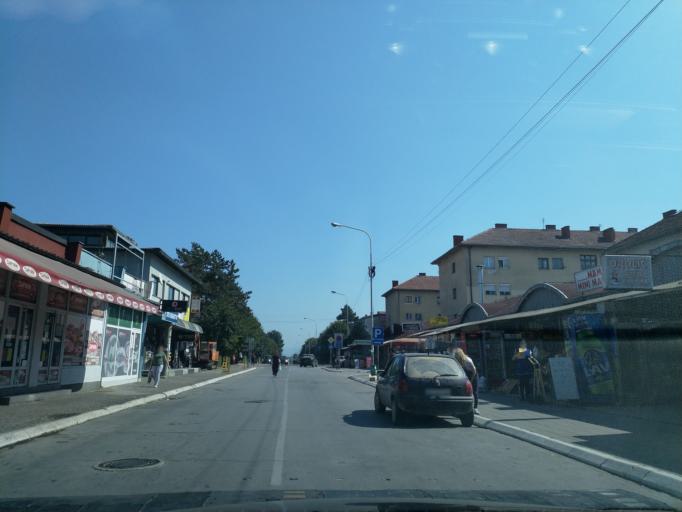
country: RS
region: Central Serbia
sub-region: Rasinski Okrug
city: Trstenik
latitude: 43.6181
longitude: 21.0060
